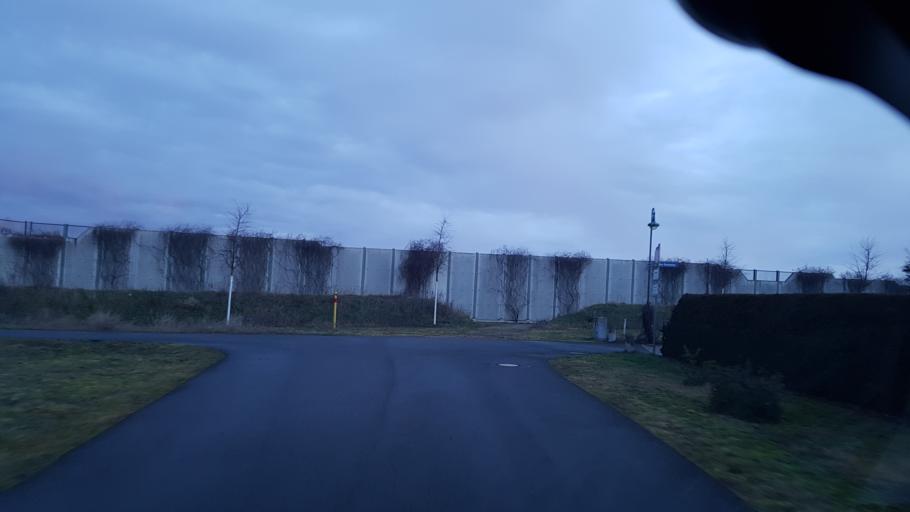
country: DE
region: Brandenburg
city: Stahnsdorf
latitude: 52.3701
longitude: 13.1930
